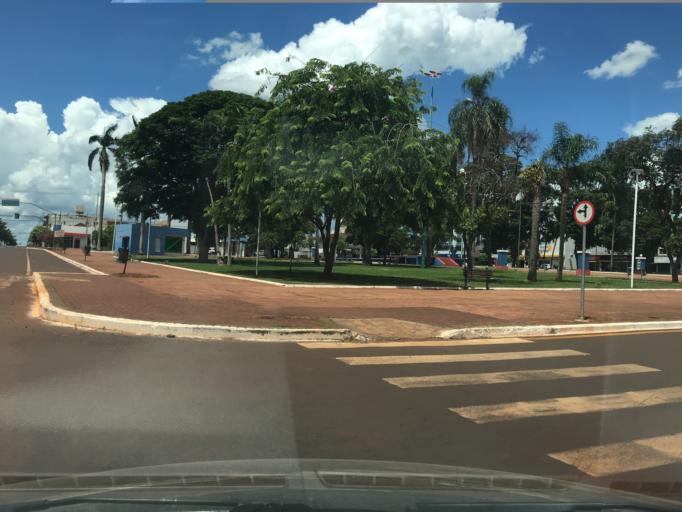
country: BR
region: Parana
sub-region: Palotina
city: Palotina
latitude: -24.2837
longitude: -53.8413
